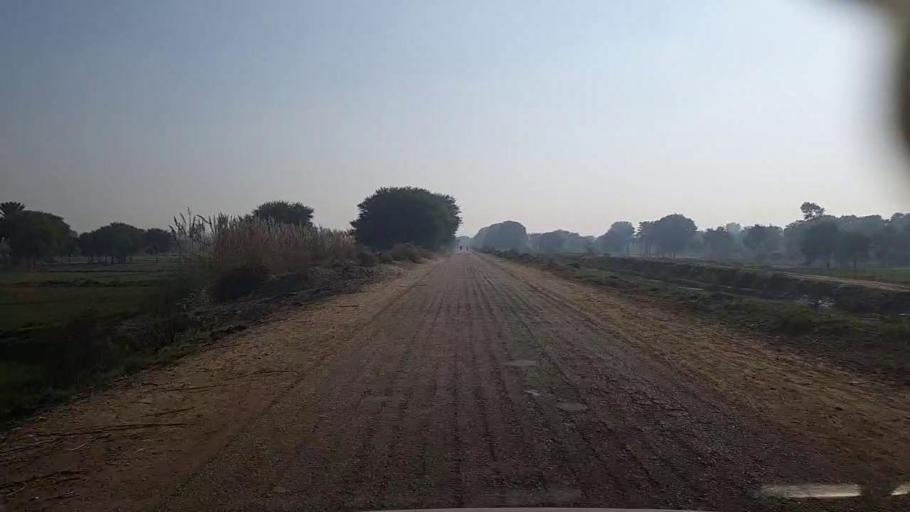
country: PK
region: Sindh
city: Kandiari
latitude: 26.8433
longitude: 68.4894
